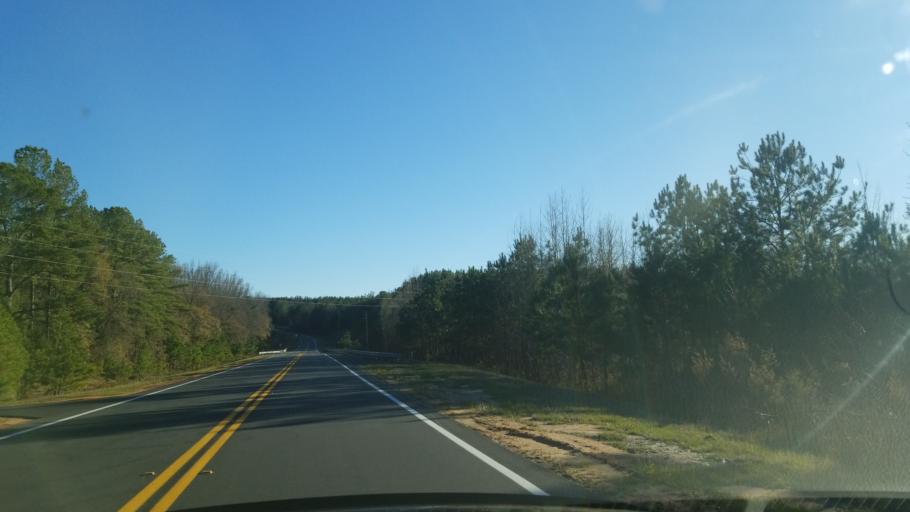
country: US
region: Georgia
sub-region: Talbot County
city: Talbotton
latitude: 32.5516
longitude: -84.5335
